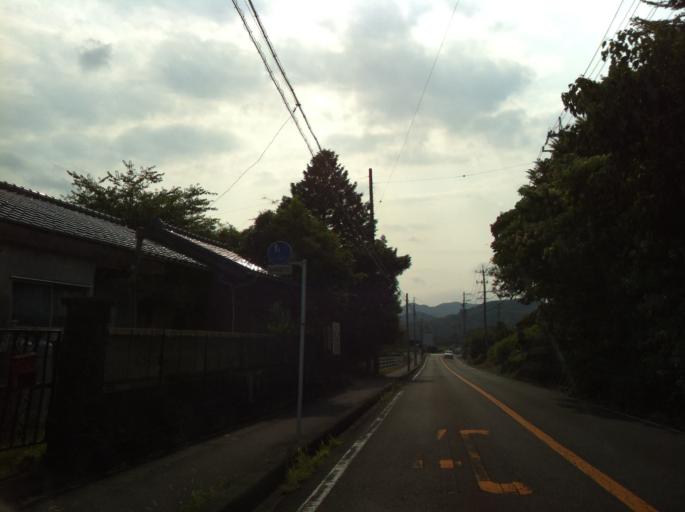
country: JP
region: Shizuoka
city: Fujieda
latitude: 34.9094
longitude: 138.2773
